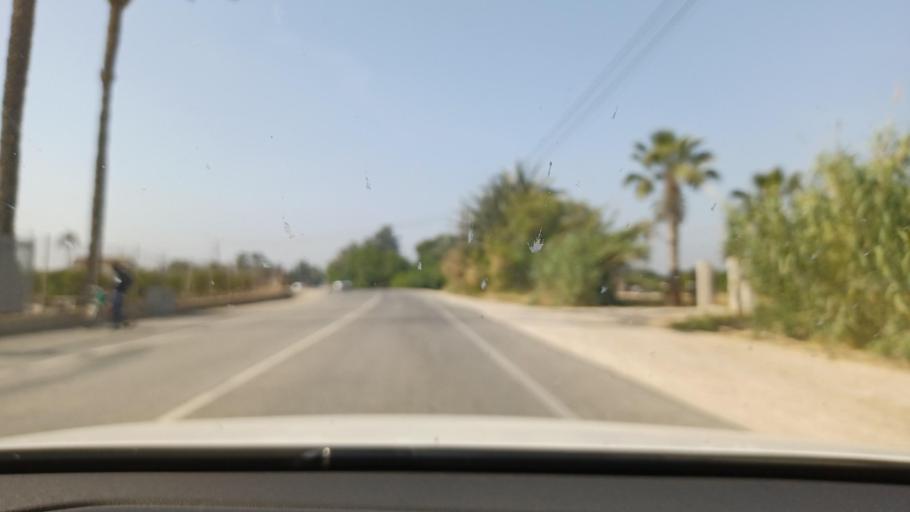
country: ES
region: Valencia
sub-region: Provincia de Alicante
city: Elche
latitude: 38.2247
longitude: -0.7189
